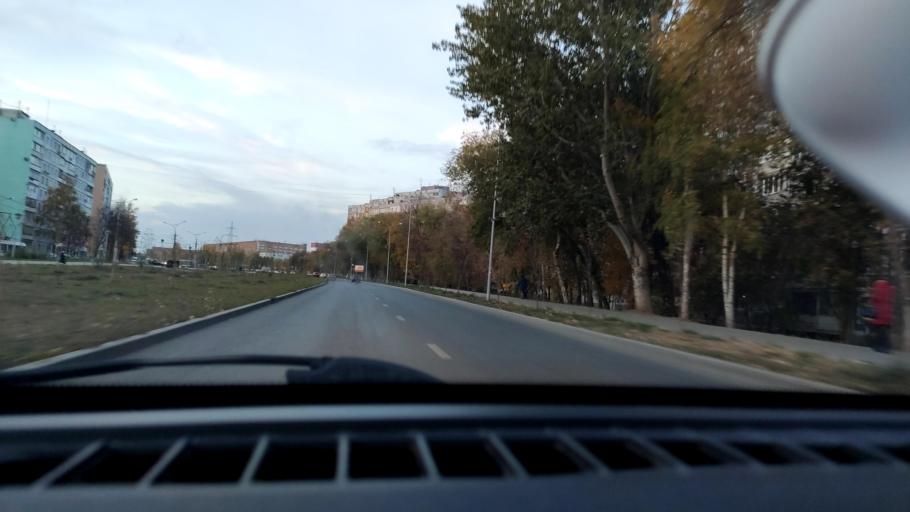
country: RU
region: Samara
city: Samara
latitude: 53.2519
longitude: 50.2477
